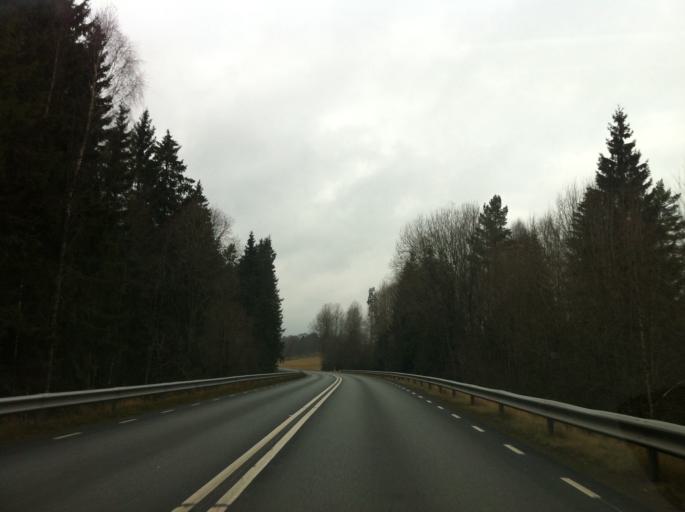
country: SE
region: Joenkoeping
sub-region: Vetlanda Kommun
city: Landsbro
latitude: 57.3883
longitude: 14.7850
